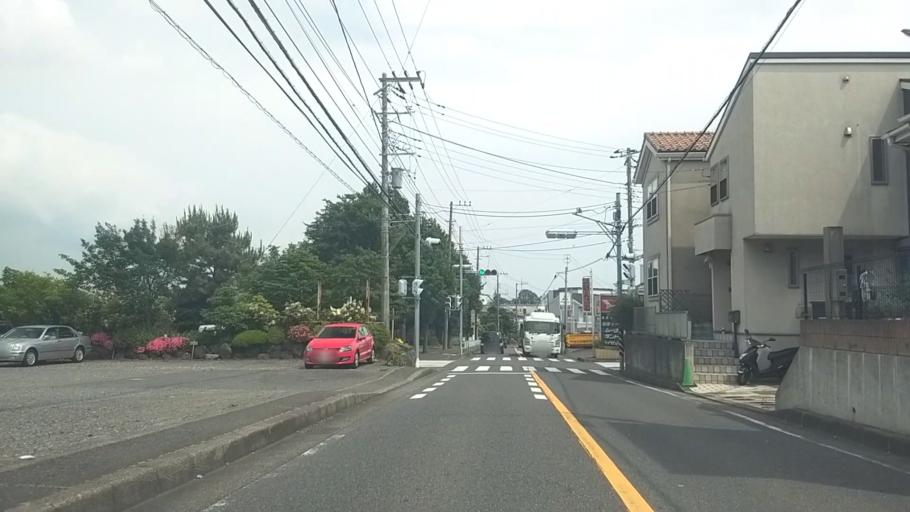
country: JP
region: Kanagawa
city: Fujisawa
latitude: 35.3934
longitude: 139.4584
